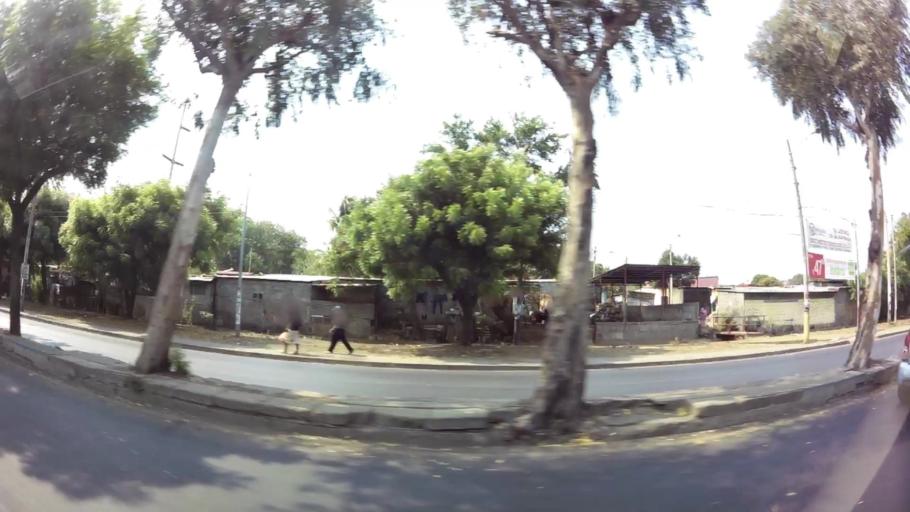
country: NI
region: Managua
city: Managua
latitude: 12.1248
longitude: -86.3023
